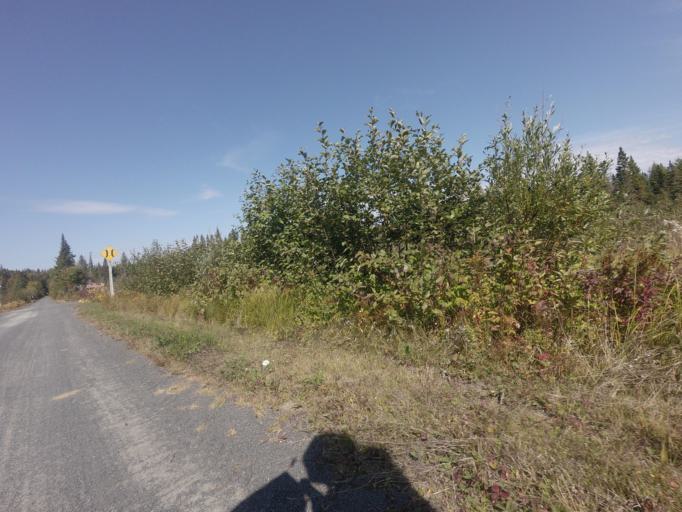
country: CA
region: Quebec
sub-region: Laurentides
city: Sainte-Agathe-des-Monts
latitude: 46.0883
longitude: -74.3425
